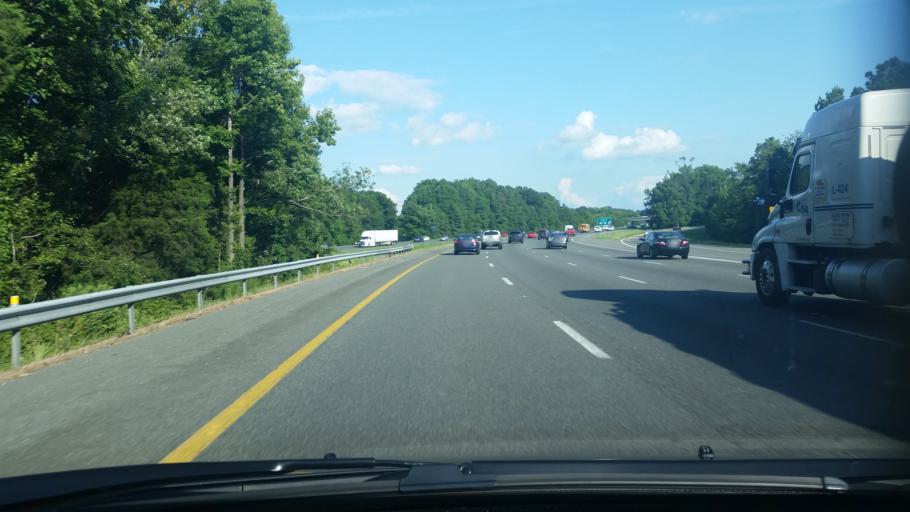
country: US
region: Virginia
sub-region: Henrico County
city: Chamberlayne
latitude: 37.6506
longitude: -77.4190
